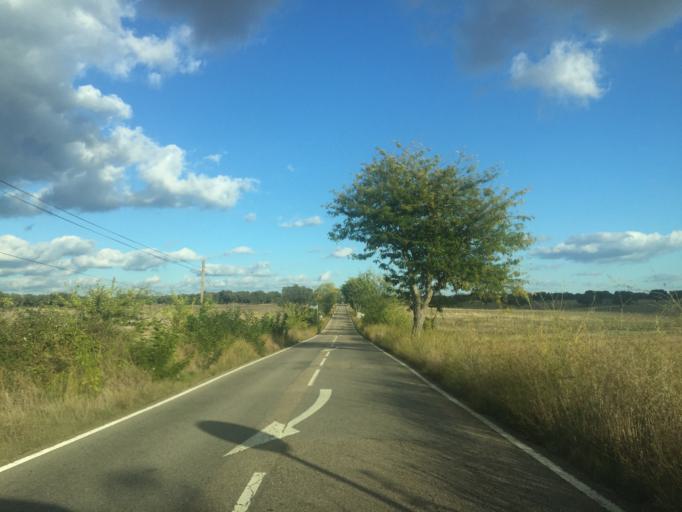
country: PT
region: Portalegre
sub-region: Alter do Chao
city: Alter do Chao
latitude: 39.2035
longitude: -7.7554
